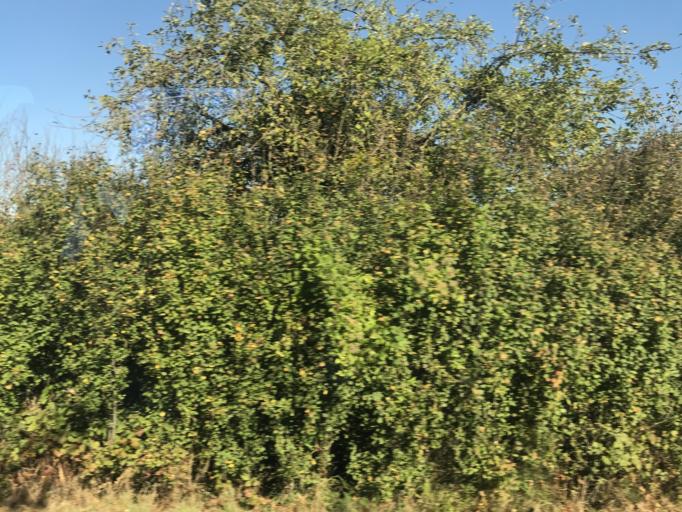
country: DE
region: Baden-Wuerttemberg
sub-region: Karlsruhe Region
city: Philippsburg
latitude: 49.2356
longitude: 8.4394
